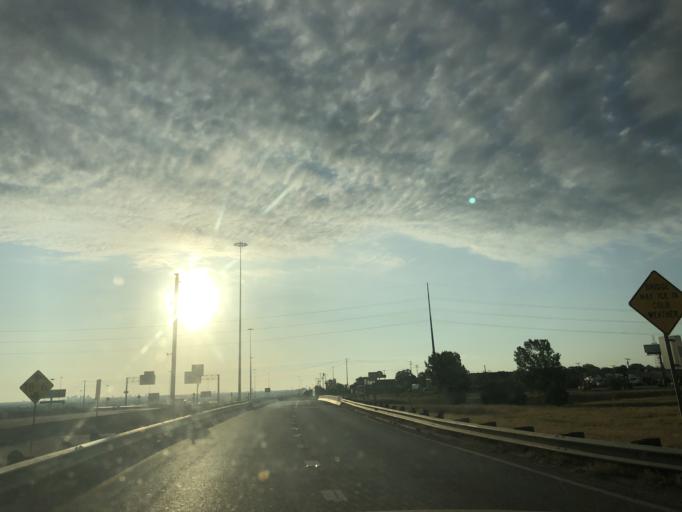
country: US
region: Texas
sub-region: Dallas County
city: Irving
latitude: 32.8365
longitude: -96.9161
